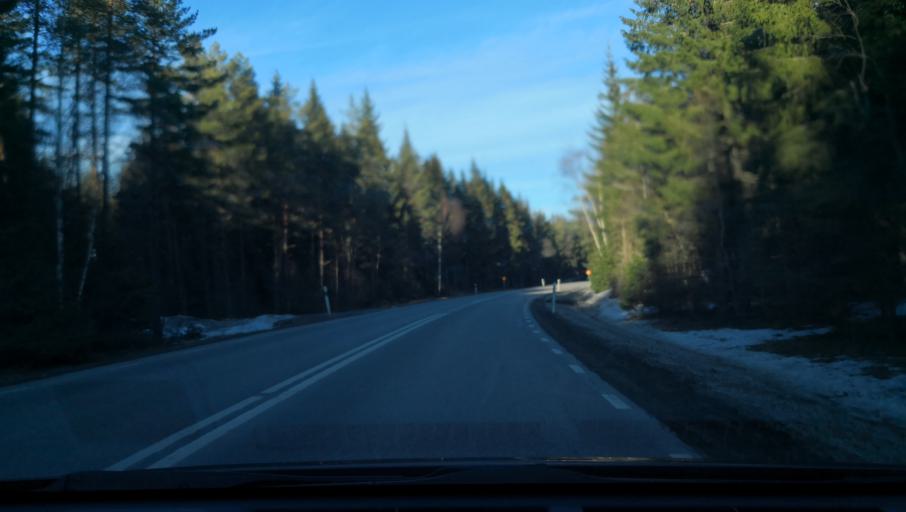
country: SE
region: Uppsala
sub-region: Osthammars Kommun
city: Gimo
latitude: 60.2139
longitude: 18.1932
